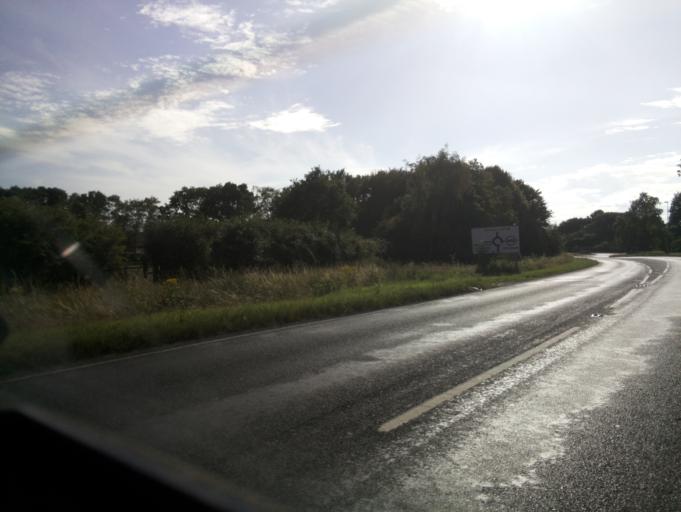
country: GB
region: England
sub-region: Hampshire
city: Romsey
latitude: 50.9848
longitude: -1.4603
